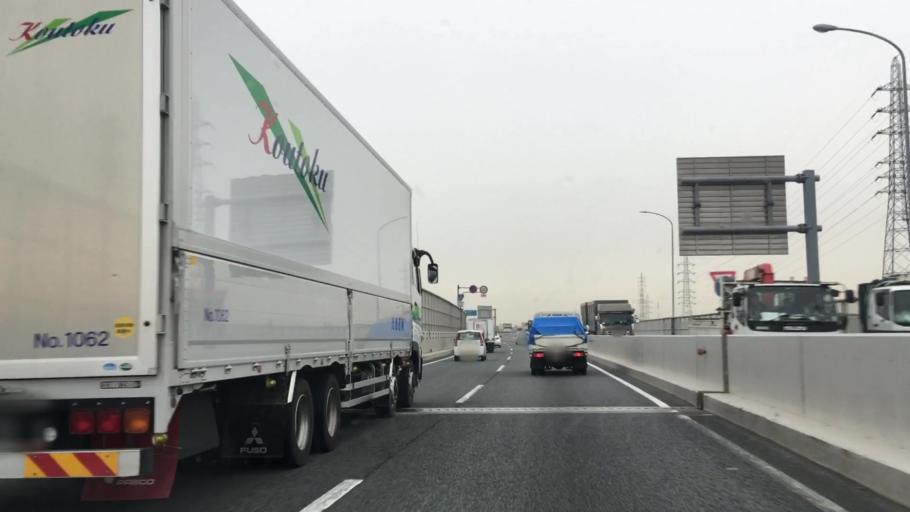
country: JP
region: Aichi
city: Chiryu
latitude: 34.9994
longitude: 137.0294
